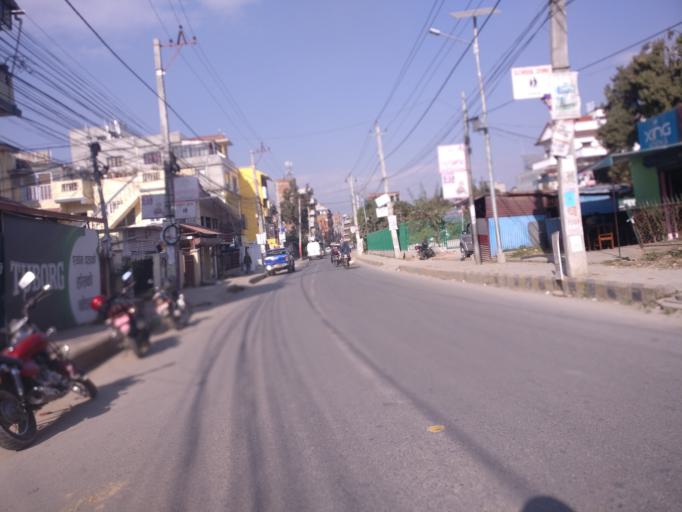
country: NP
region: Central Region
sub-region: Bagmati Zone
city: Patan
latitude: 27.6756
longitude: 85.3082
